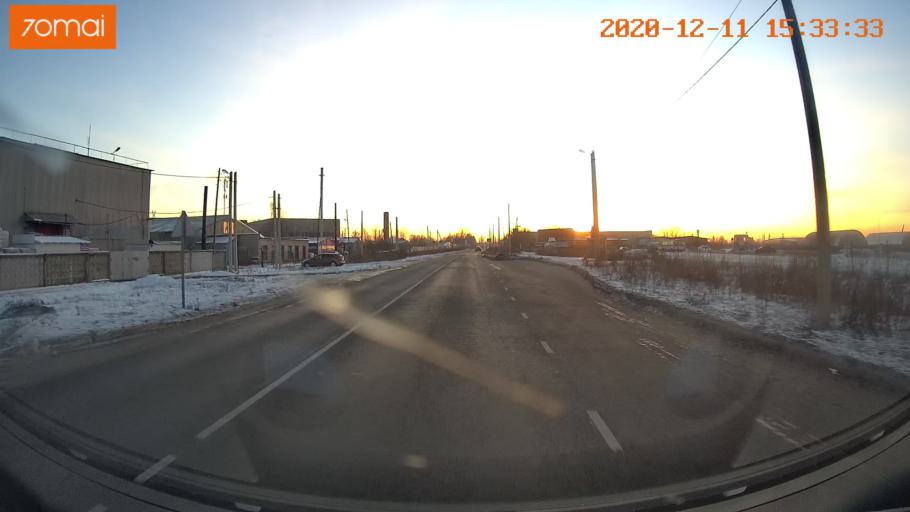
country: RU
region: Ivanovo
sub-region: Gorod Ivanovo
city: Ivanovo
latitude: 57.0511
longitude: 40.9471
